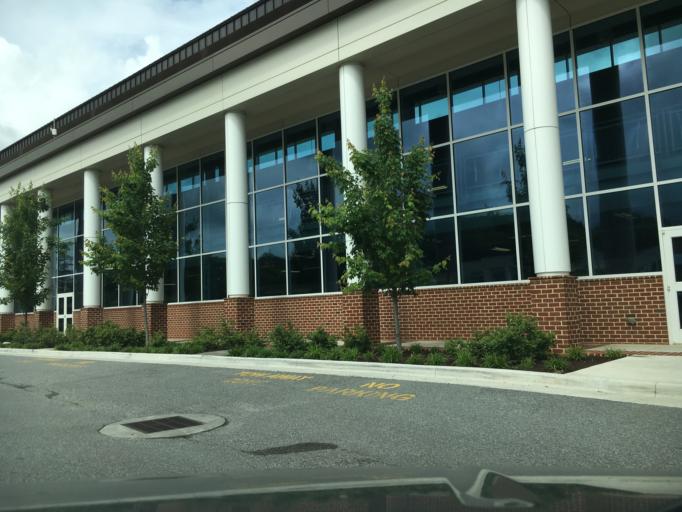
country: US
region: Virginia
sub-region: City of Lynchburg
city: West Lynchburg
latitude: 37.3573
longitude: -79.1730
